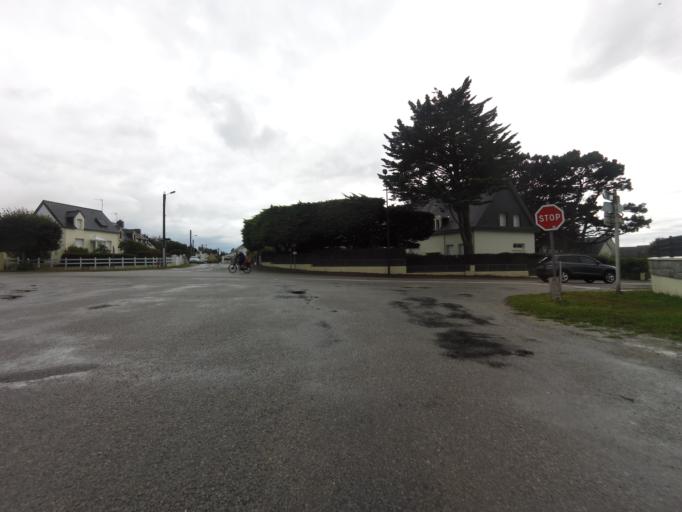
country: FR
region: Brittany
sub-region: Departement du Morbihan
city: Etel
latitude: 47.6621
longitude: -3.2053
